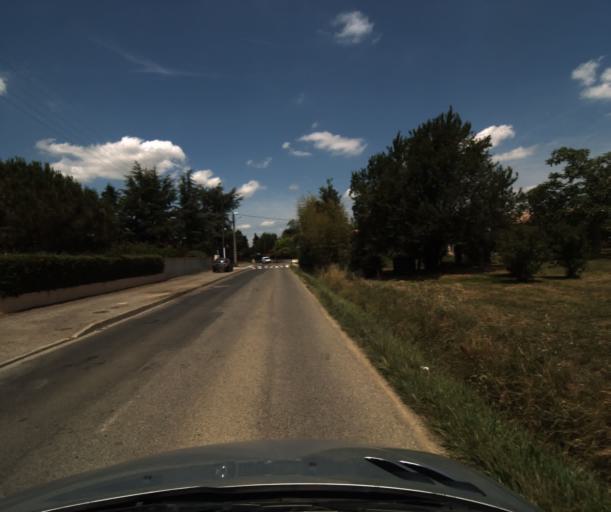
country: FR
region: Midi-Pyrenees
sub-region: Departement de la Haute-Garonne
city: Saint-Lys
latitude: 43.5098
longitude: 1.1801
